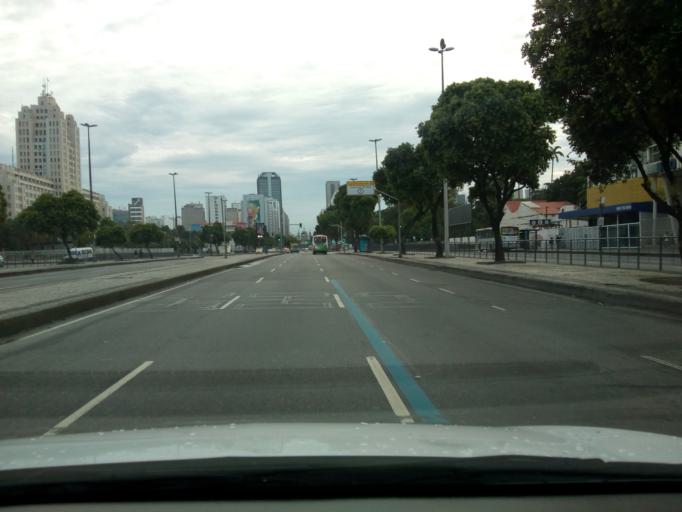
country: BR
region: Rio de Janeiro
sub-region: Rio De Janeiro
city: Rio de Janeiro
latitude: -22.9056
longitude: -43.1923
